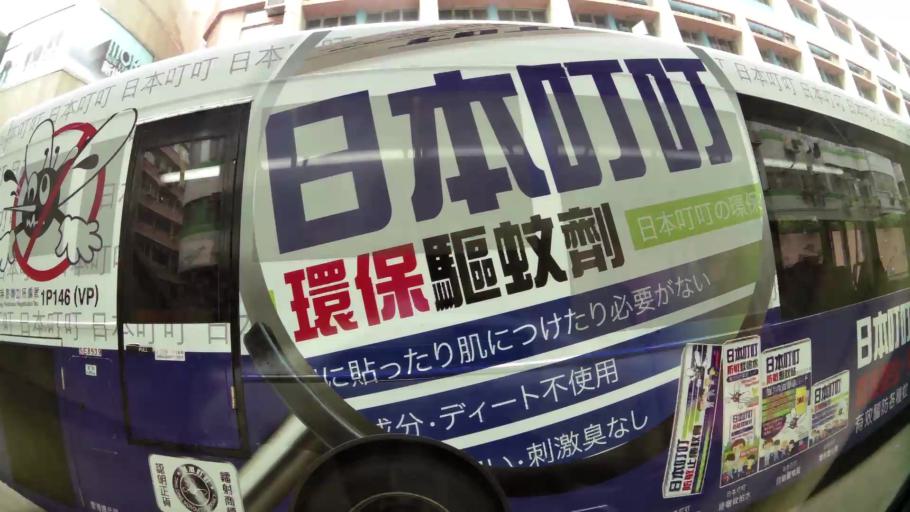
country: HK
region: Kowloon City
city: Kowloon
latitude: 22.3223
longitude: 114.1711
